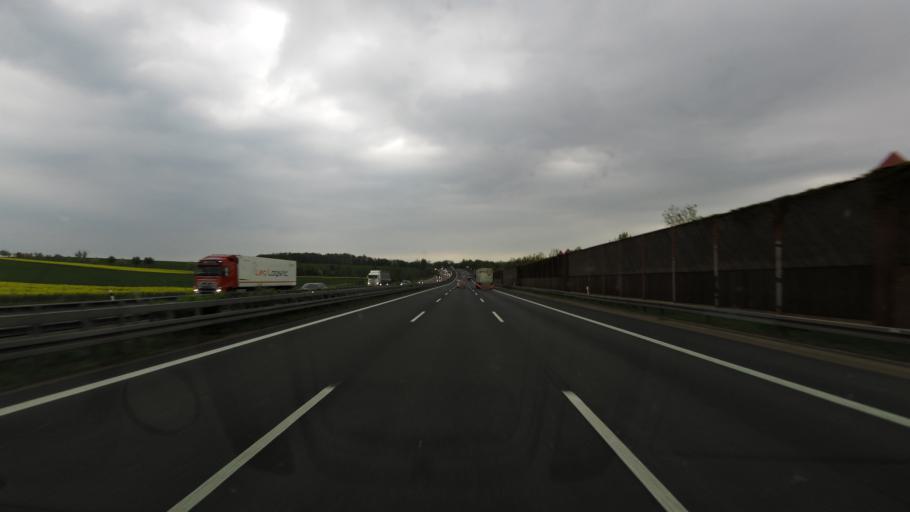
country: DE
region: Saxony
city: Reinsberg
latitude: 51.0500
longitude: 13.3523
